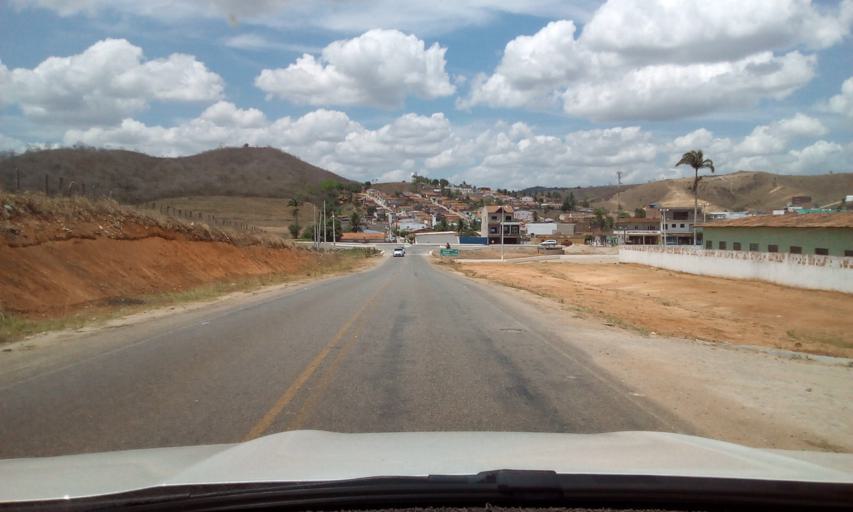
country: BR
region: Paraiba
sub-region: Alagoinha
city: Alagoinha
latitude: -6.9555
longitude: -35.5445
